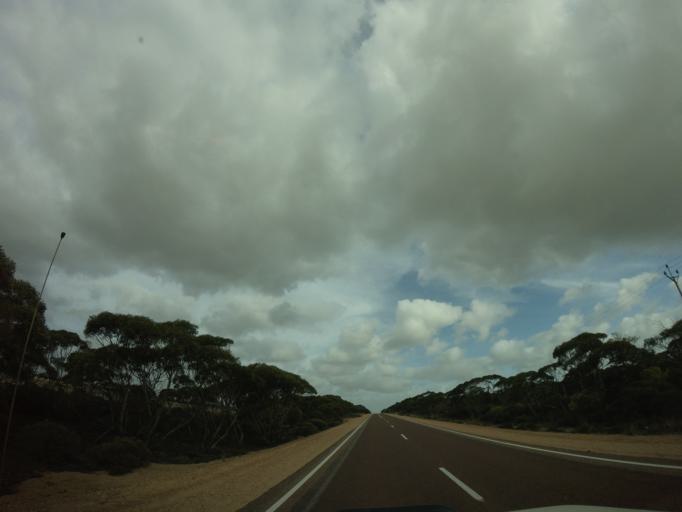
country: AU
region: South Australia
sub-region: Ceduna
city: Ceduna
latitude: -32.0543
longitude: 133.6057
